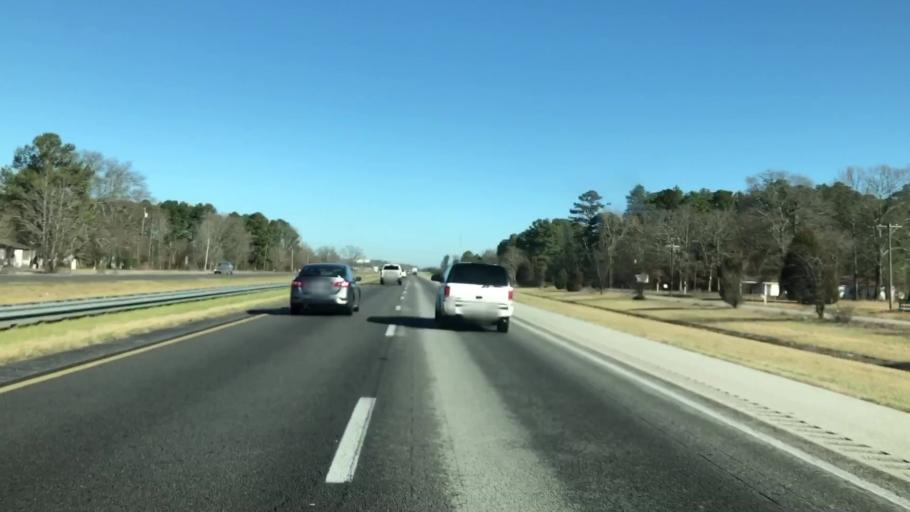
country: US
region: Alabama
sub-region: Limestone County
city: Athens
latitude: 34.8680
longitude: -86.9237
